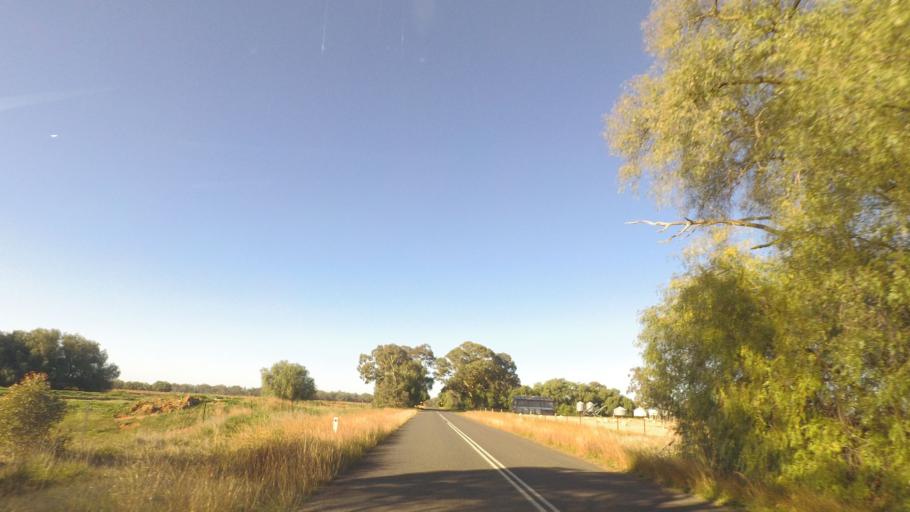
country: AU
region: Victoria
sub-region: Greater Bendigo
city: Epsom
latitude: -36.6466
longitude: 144.5341
